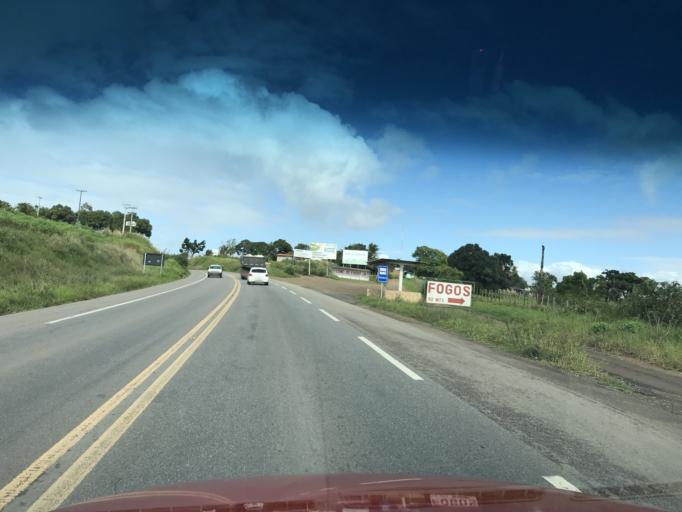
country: BR
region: Bahia
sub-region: Conceicao Do Almeida
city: Muritiba
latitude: -12.8952
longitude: -39.2339
